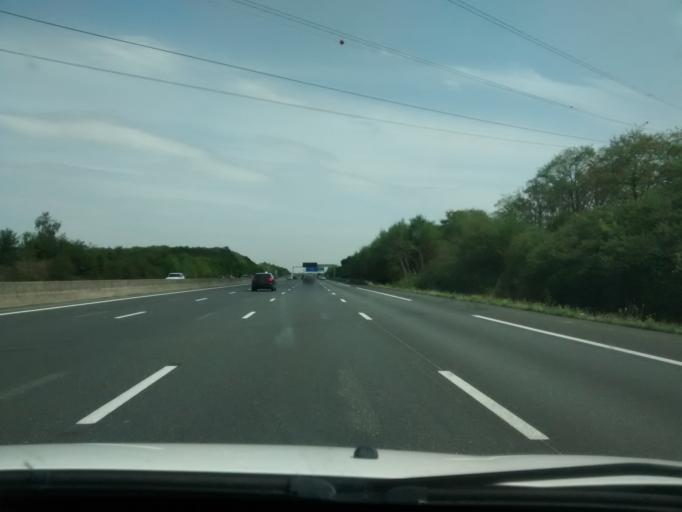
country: FR
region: Ile-de-France
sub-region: Departement de l'Essonne
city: Fontenay-les-Briis
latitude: 48.6424
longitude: 2.1574
